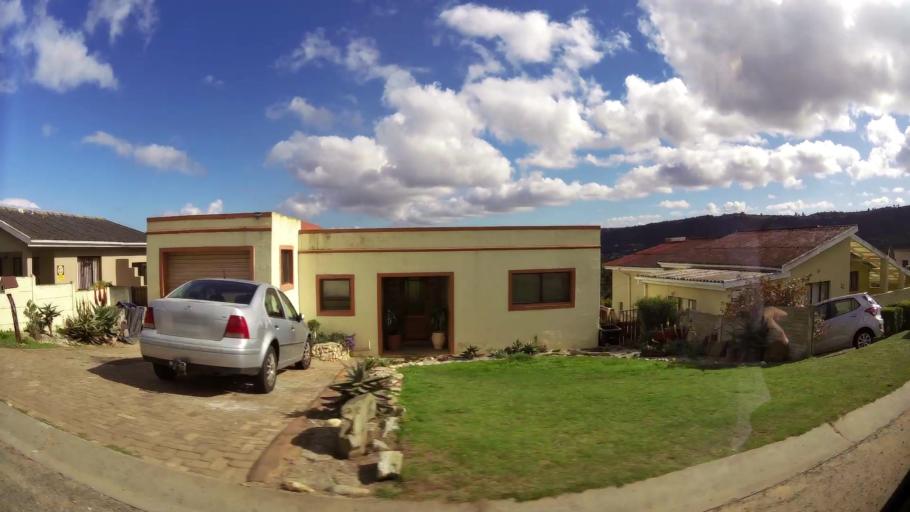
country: ZA
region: Western Cape
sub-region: Eden District Municipality
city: Knysna
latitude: -34.0499
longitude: 23.0825
